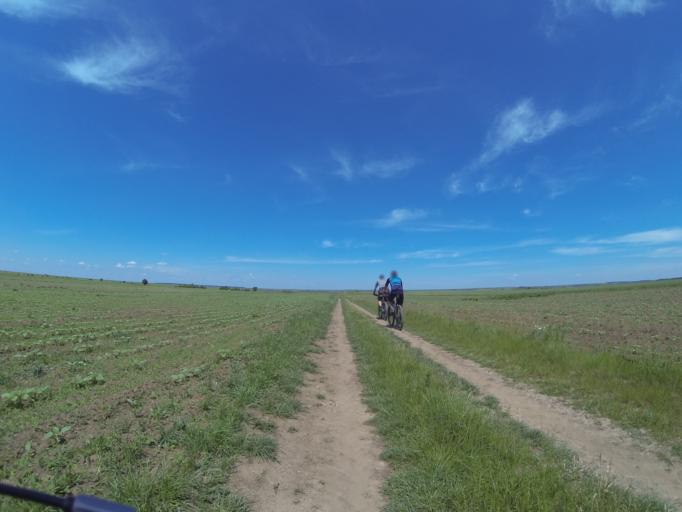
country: RO
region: Dolj
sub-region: Comuna Teslui
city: Teslui
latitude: 44.1952
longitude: 24.1392
